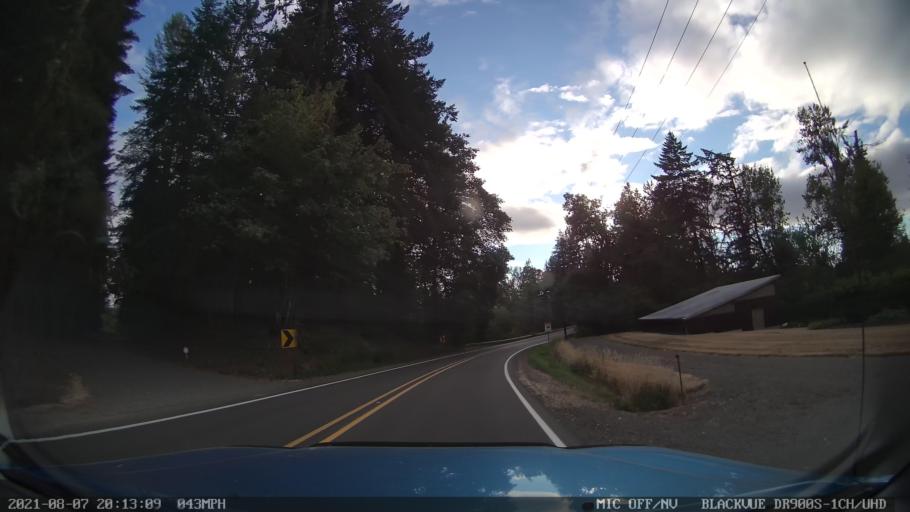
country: US
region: Oregon
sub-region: Marion County
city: Hayesville
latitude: 44.9564
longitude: -122.9195
